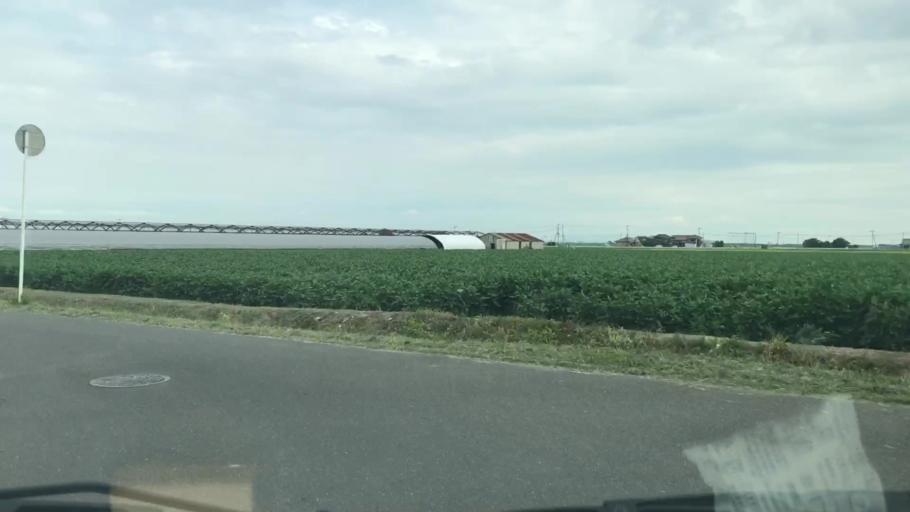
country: JP
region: Saga Prefecture
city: Saga-shi
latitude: 33.2904
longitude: 130.2303
